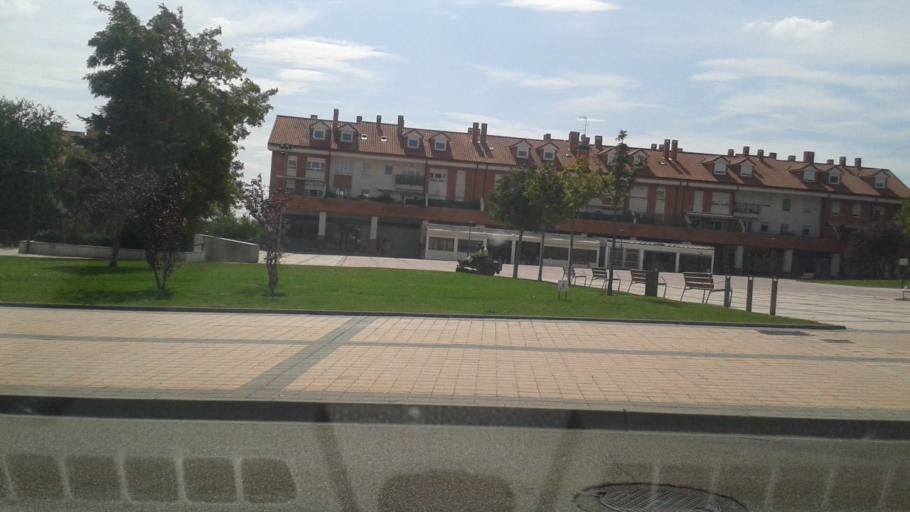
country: ES
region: Castille and Leon
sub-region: Provincia de Valladolid
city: Arroyo
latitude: 41.6261
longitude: -4.7731
